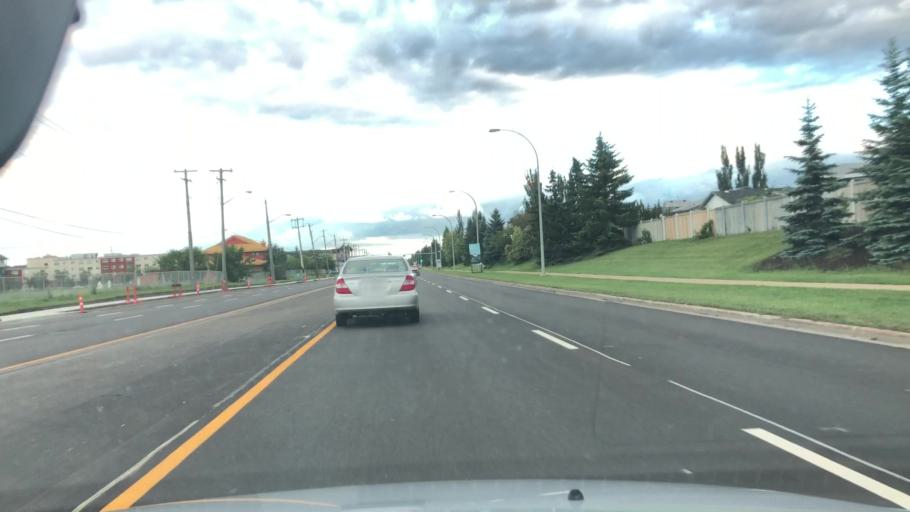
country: CA
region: Alberta
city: St. Albert
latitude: 53.6133
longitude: -113.5413
